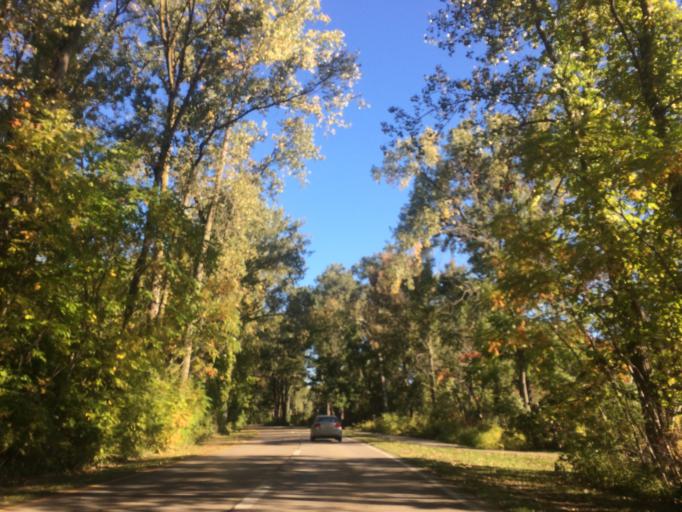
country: US
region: Pennsylvania
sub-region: Erie County
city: Erie
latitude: 42.1274
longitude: -80.1450
